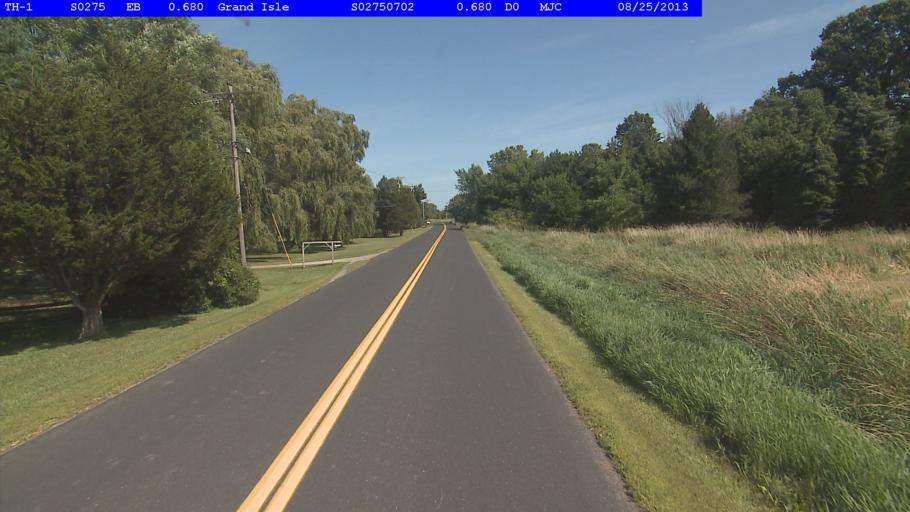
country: US
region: New York
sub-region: Clinton County
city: Cumberland Head
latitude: 44.7102
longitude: -73.3426
